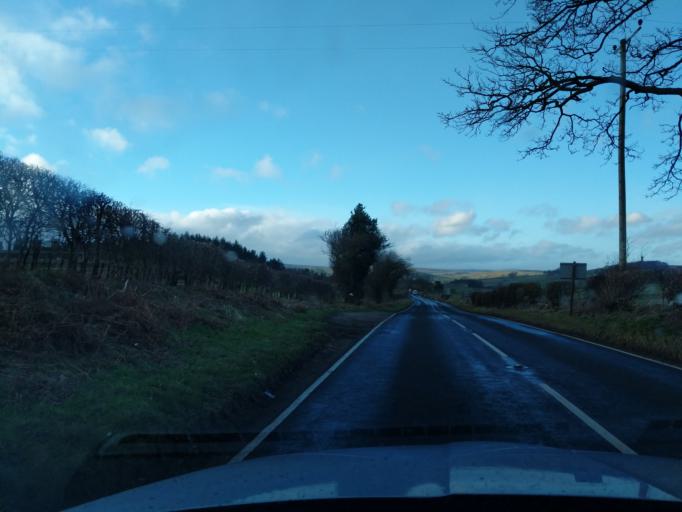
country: GB
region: England
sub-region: North Yorkshire
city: Leyburn
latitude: 54.3503
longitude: -1.8080
